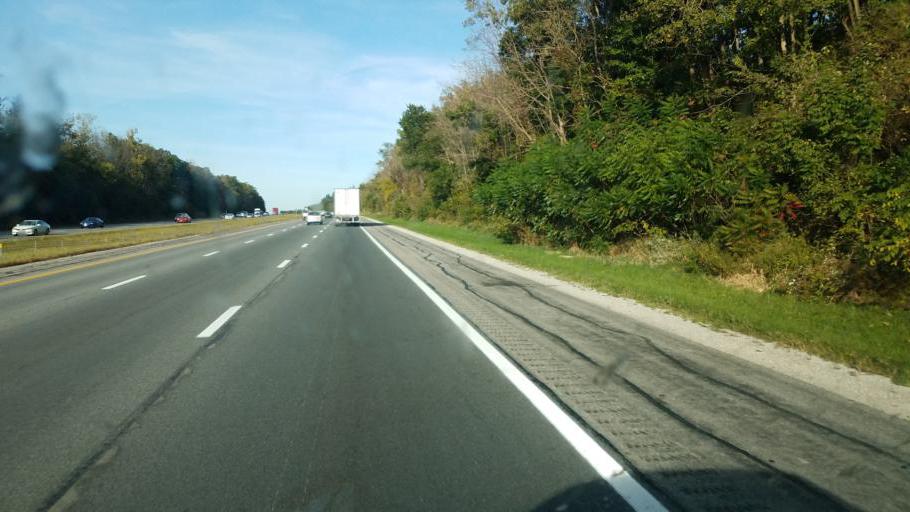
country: US
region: Ohio
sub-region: Richland County
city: Lincoln Heights
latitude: 40.7574
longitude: -82.4337
